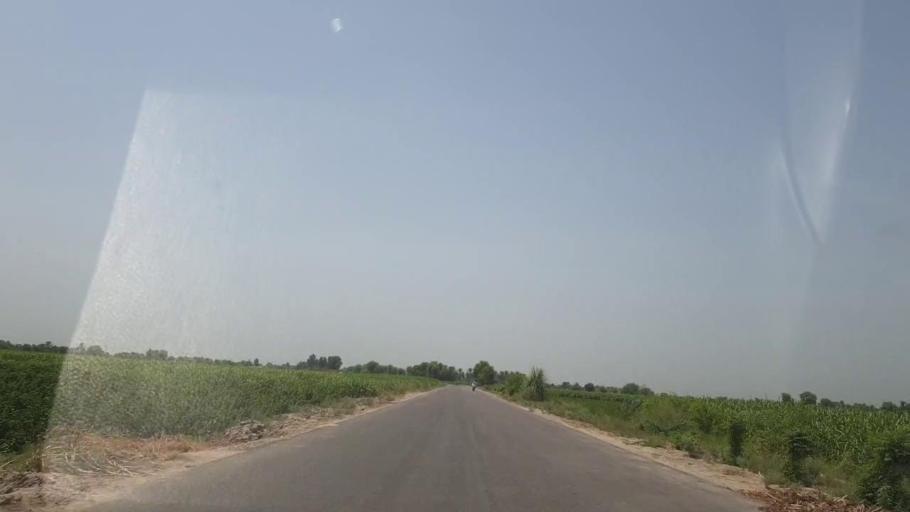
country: PK
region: Sindh
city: Ranipur
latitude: 27.2957
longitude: 68.6050
